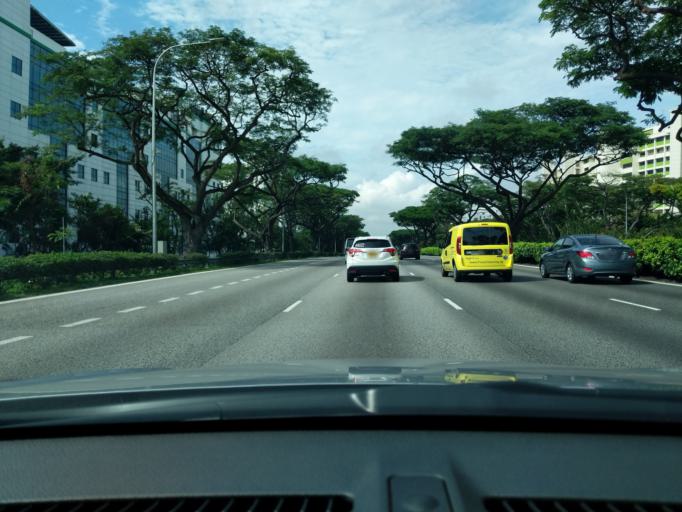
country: SG
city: Singapore
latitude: 1.3311
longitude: 103.9170
